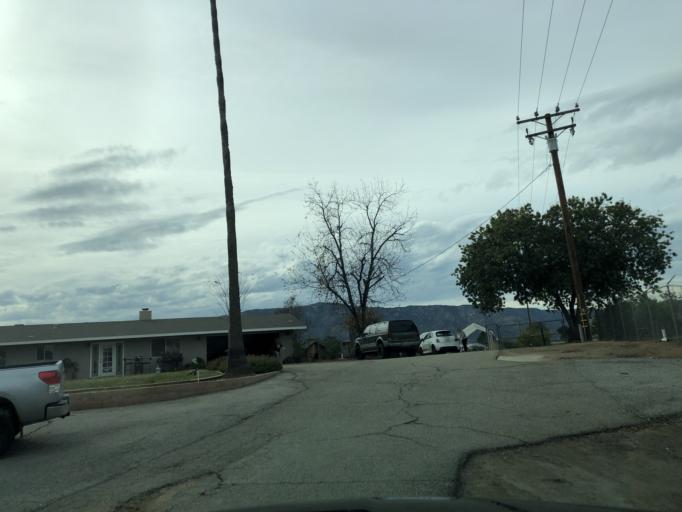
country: US
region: California
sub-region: Riverside County
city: Wildomar
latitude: 33.6233
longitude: -117.2677
